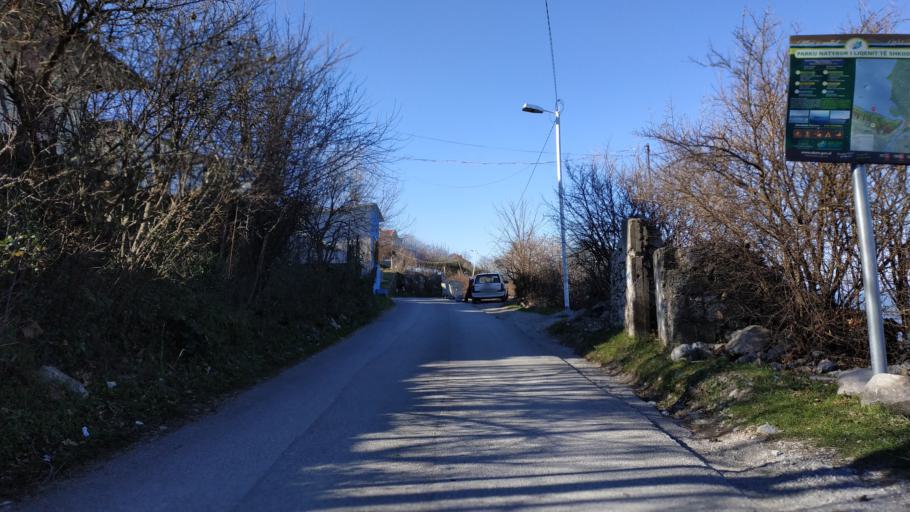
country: AL
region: Shkoder
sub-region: Rrethi i Shkodres
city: Berdica e Madhe
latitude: 42.0597
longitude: 19.4527
